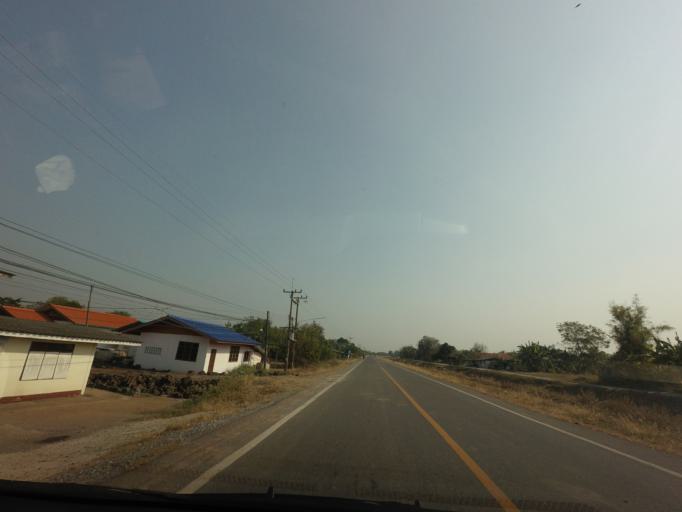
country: TH
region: Chachoengsao
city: Khlong Khuean
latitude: 13.8036
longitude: 101.1738
